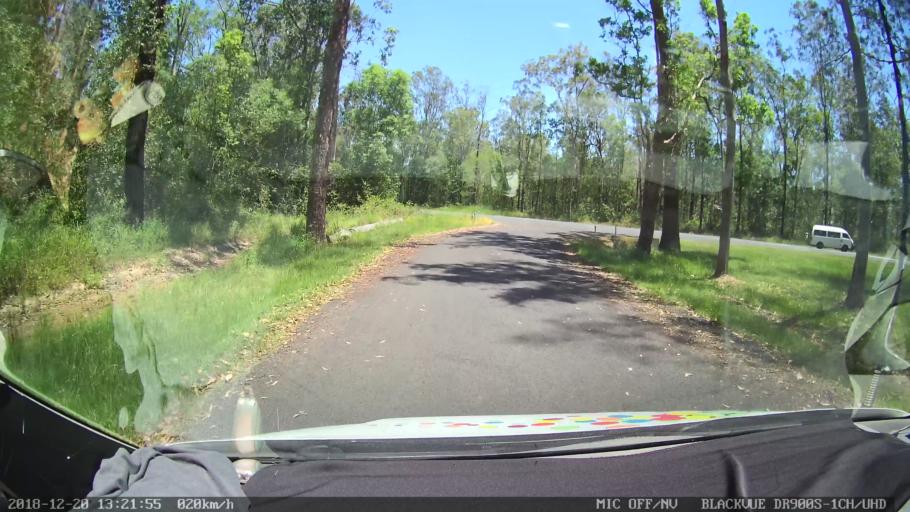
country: AU
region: New South Wales
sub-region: Richmond Valley
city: Casino
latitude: -29.0885
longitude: 153.0016
